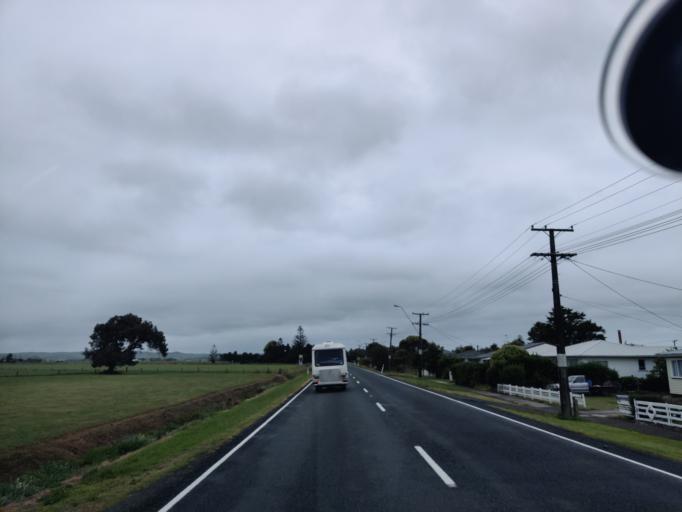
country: NZ
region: Northland
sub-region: Kaipara District
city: Dargaville
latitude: -36.1303
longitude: 174.0333
